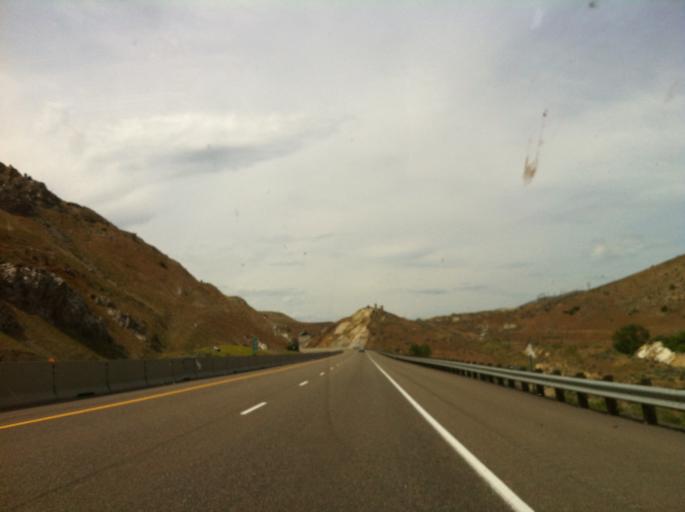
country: US
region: Idaho
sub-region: Washington County
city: Weiser
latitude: 44.3720
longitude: -117.2963
